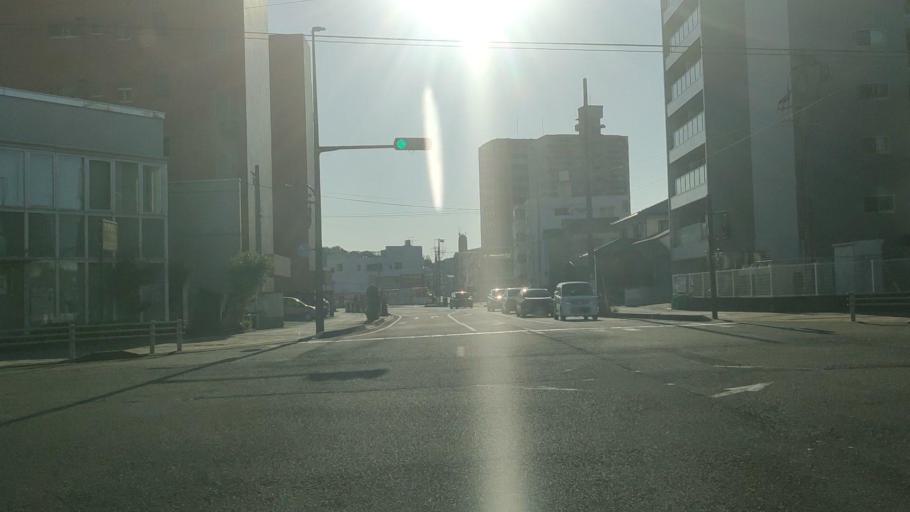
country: JP
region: Oita
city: Oita
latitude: 33.2309
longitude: 131.6018
